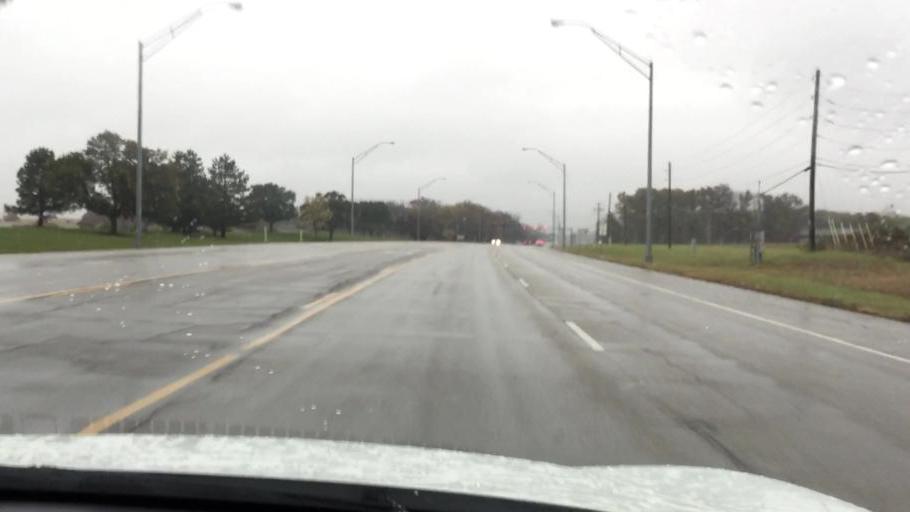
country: US
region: Ohio
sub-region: Champaign County
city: North Lewisburg
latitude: 40.2748
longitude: -83.5096
